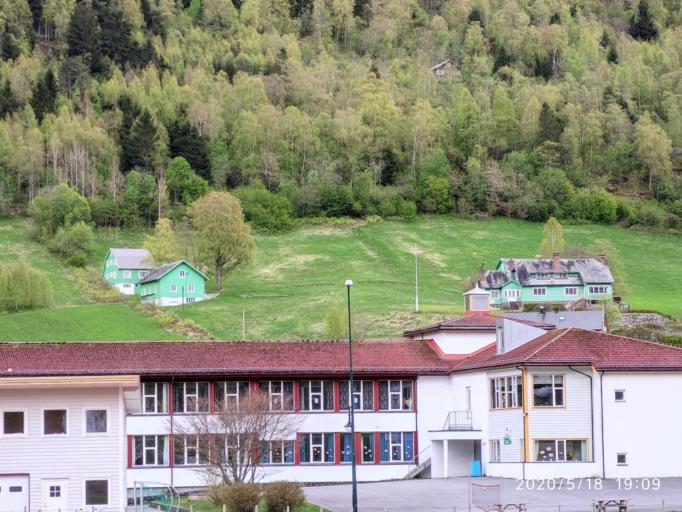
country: NO
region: Sogn og Fjordane
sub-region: Stryn
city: Stryn
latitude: 61.8341
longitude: 6.8053
